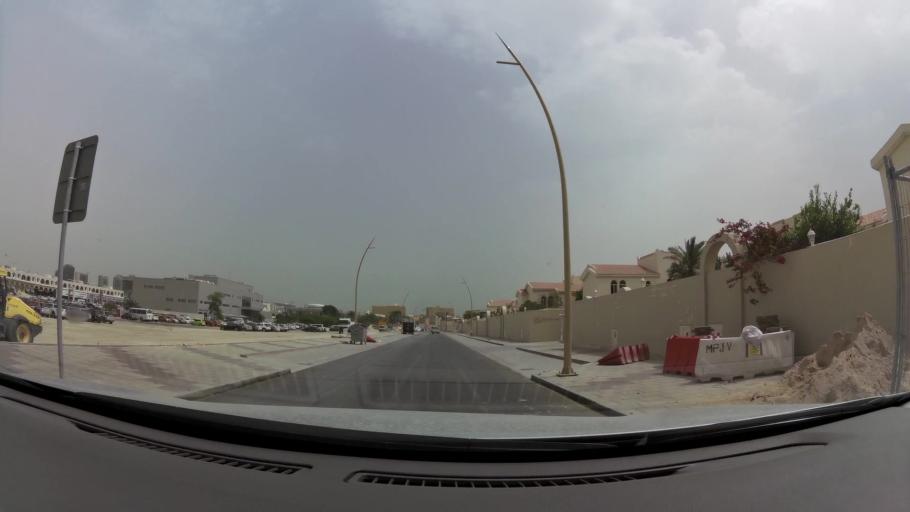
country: QA
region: Baladiyat ad Dawhah
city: Doha
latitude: 25.2672
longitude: 51.5053
